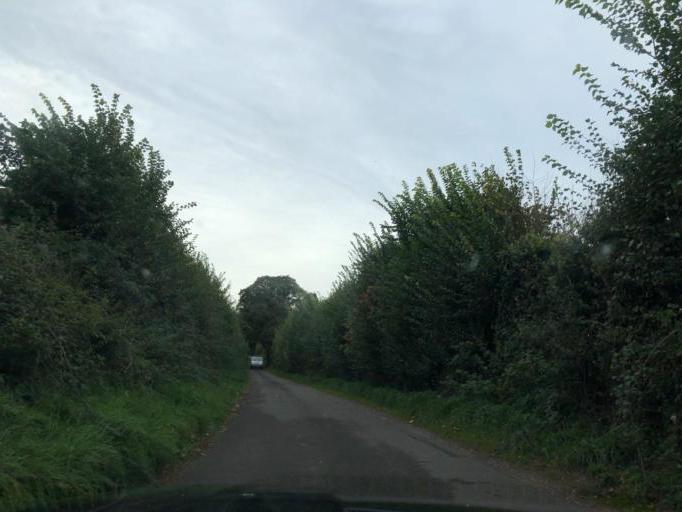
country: GB
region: England
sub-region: Warwickshire
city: Wroxall
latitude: 52.3119
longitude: -1.6574
